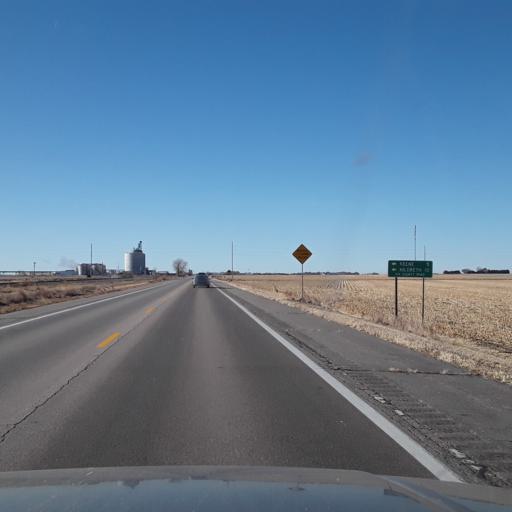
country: US
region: Nebraska
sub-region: Kearney County
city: Minden
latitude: 40.4873
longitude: -99.0616
